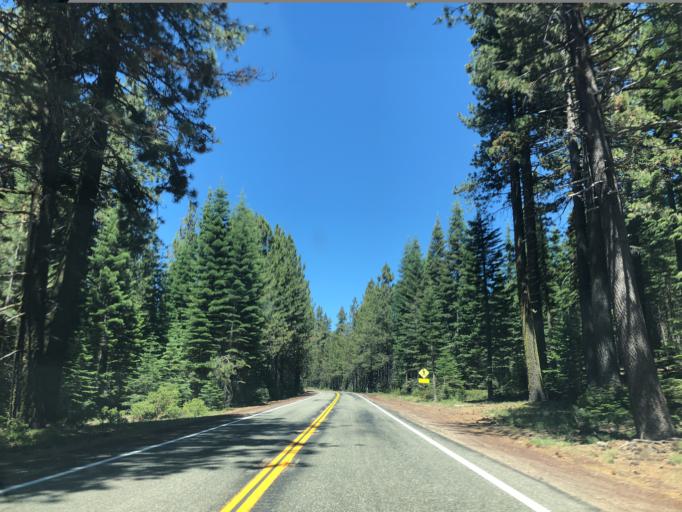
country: US
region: California
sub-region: Shasta County
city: Shingletown
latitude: 40.5558
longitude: -121.5789
